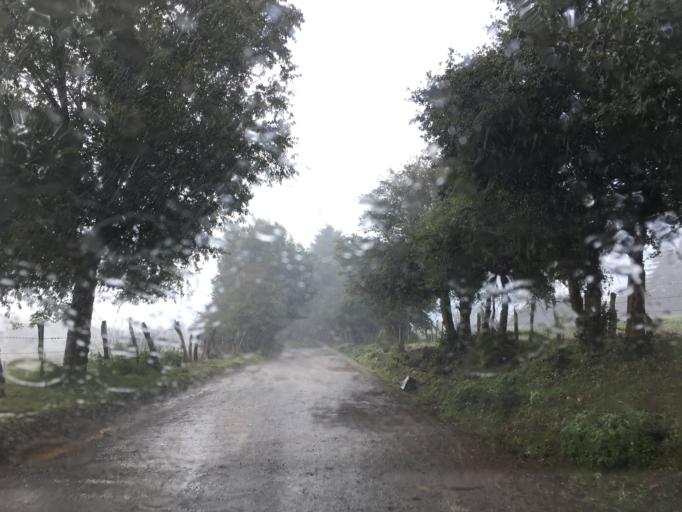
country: MX
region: Michoacan
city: Acuitzio del Canje
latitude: 19.5234
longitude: -101.2215
